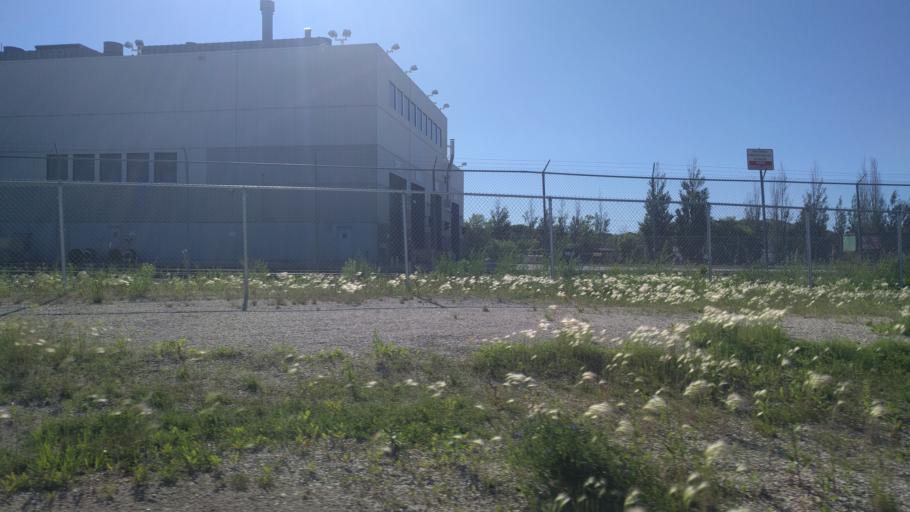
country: CA
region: Manitoba
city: Winnipeg
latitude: 49.8684
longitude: -97.1420
